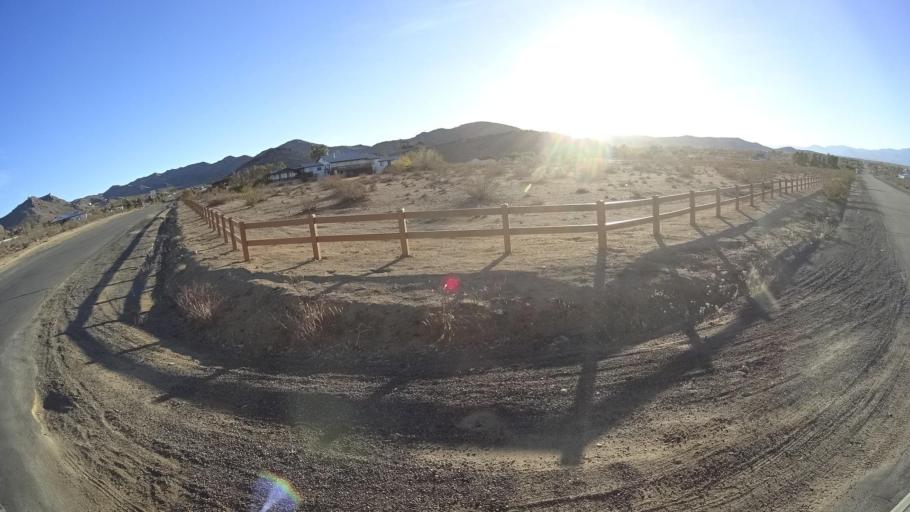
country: US
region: California
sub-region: Kern County
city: Ridgecrest
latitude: 35.5860
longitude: -117.6482
